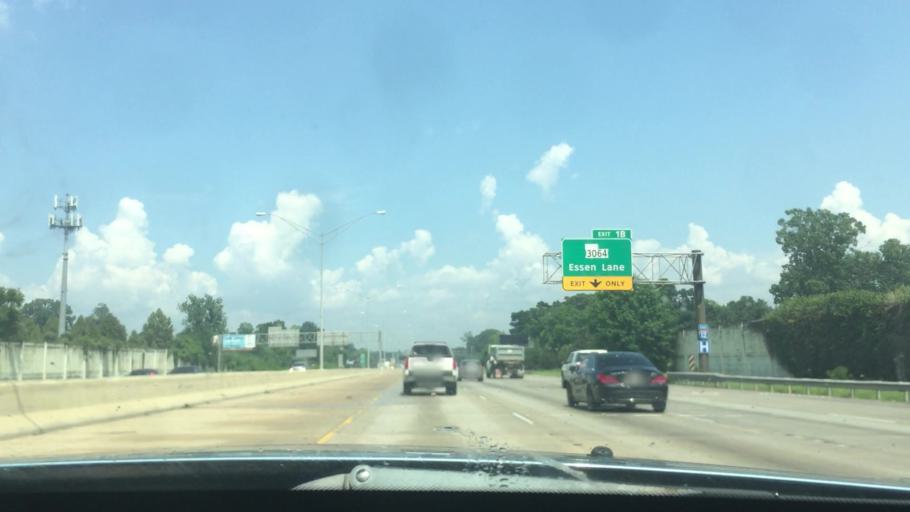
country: US
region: Louisiana
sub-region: East Baton Rouge Parish
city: Westminster
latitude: 30.4178
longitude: -91.1057
